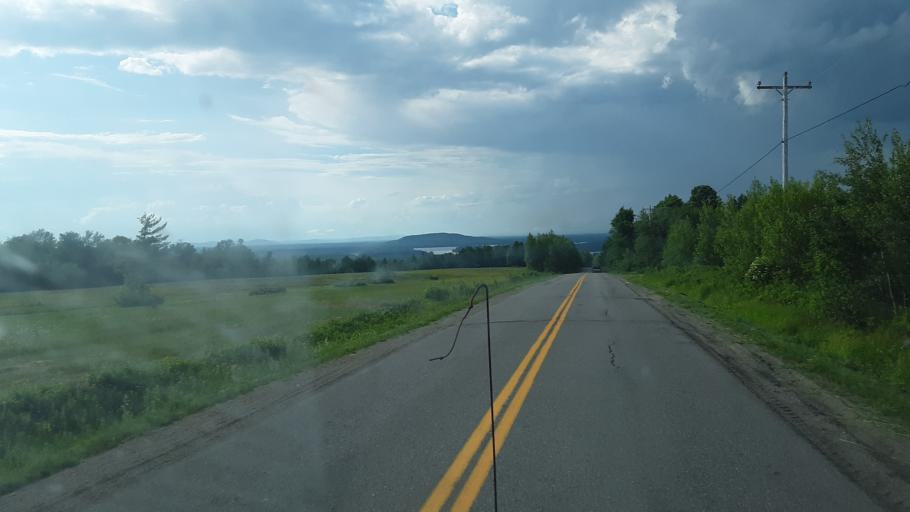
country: US
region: Maine
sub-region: Washington County
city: Calais
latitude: 45.0947
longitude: -67.5074
